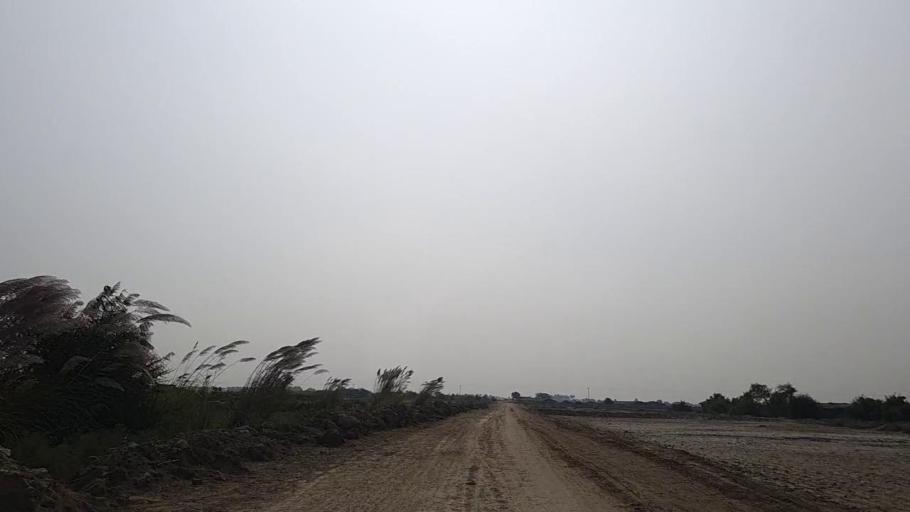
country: PK
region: Sindh
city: Mirpur Sakro
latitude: 24.6329
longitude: 67.7676
